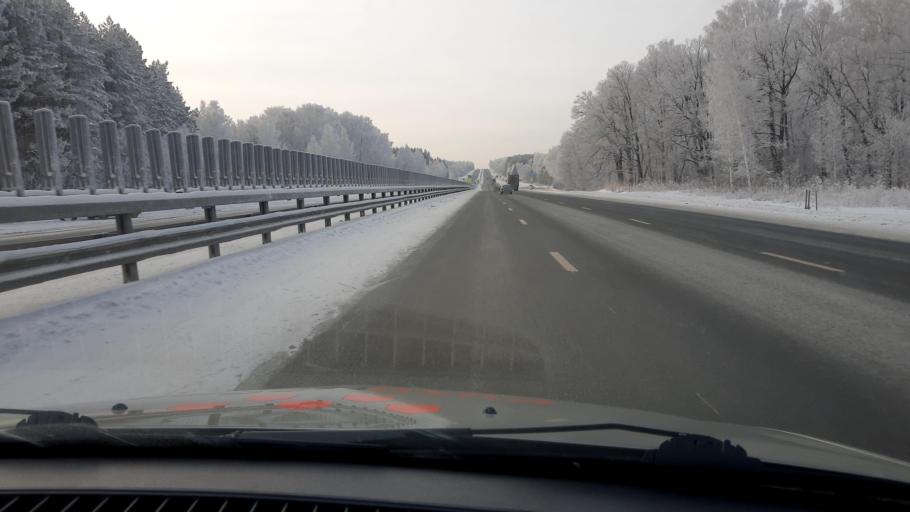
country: RU
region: Bashkortostan
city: Avdon
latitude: 54.6504
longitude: 55.6552
